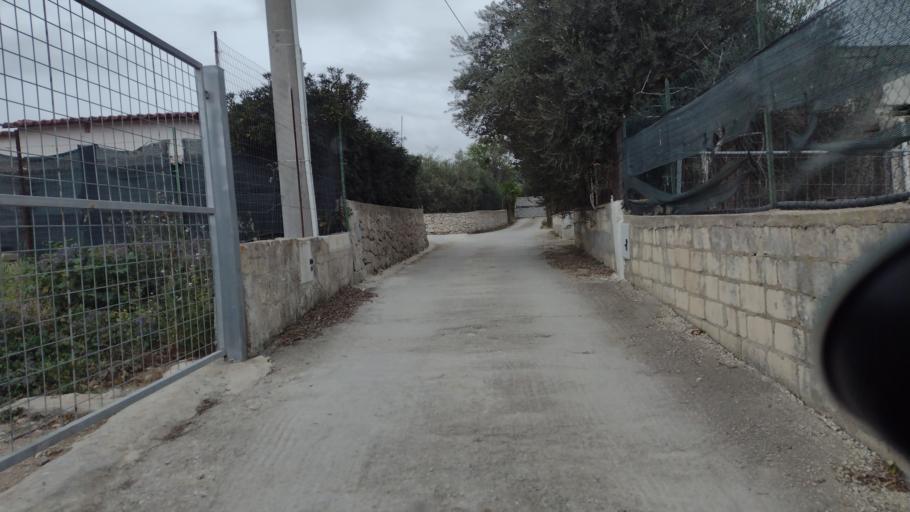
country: IT
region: Sicily
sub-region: Provincia di Siracusa
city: Avola
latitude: 36.8980
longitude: 15.1103
